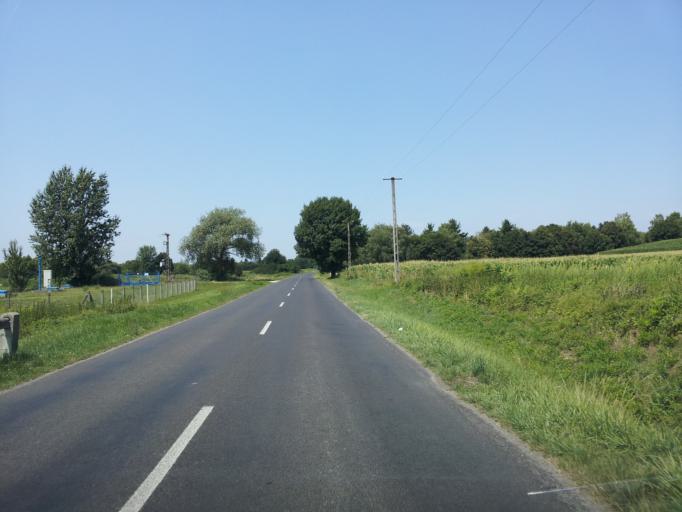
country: HU
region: Zala
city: Zalaegerszeg
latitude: 46.8578
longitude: 16.8216
